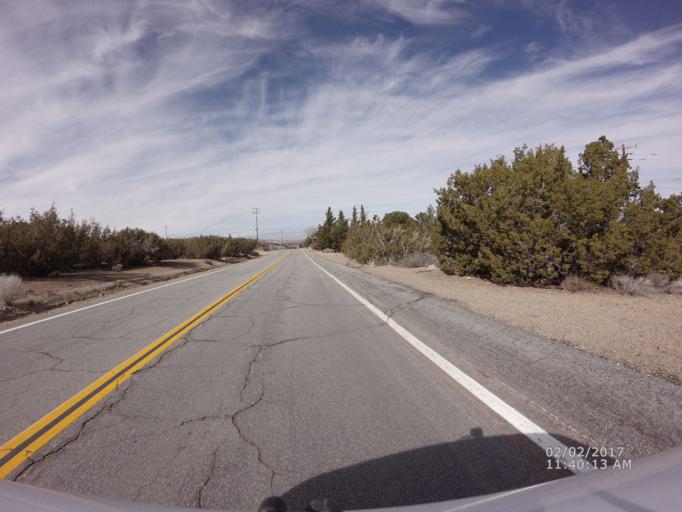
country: US
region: California
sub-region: Los Angeles County
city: Littlerock
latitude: 34.4387
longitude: -117.9317
